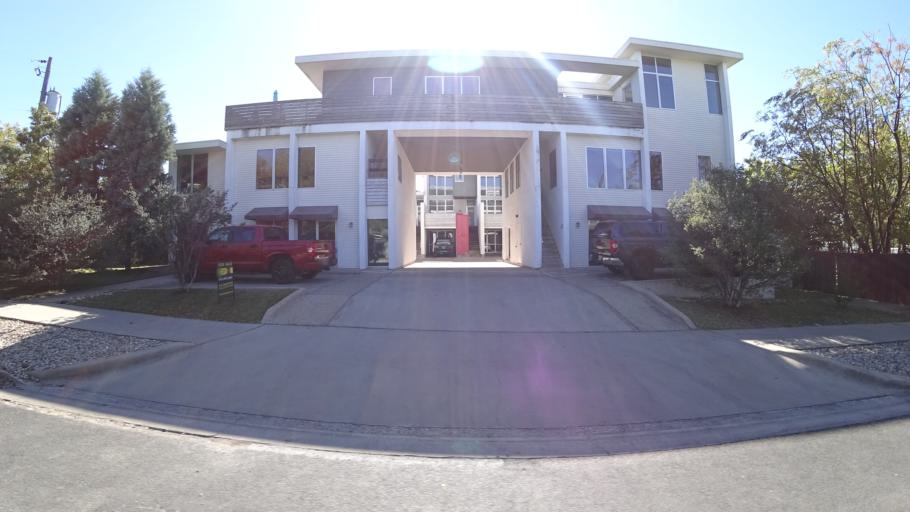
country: US
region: Texas
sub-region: Travis County
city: Austin
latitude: 30.3233
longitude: -97.7385
